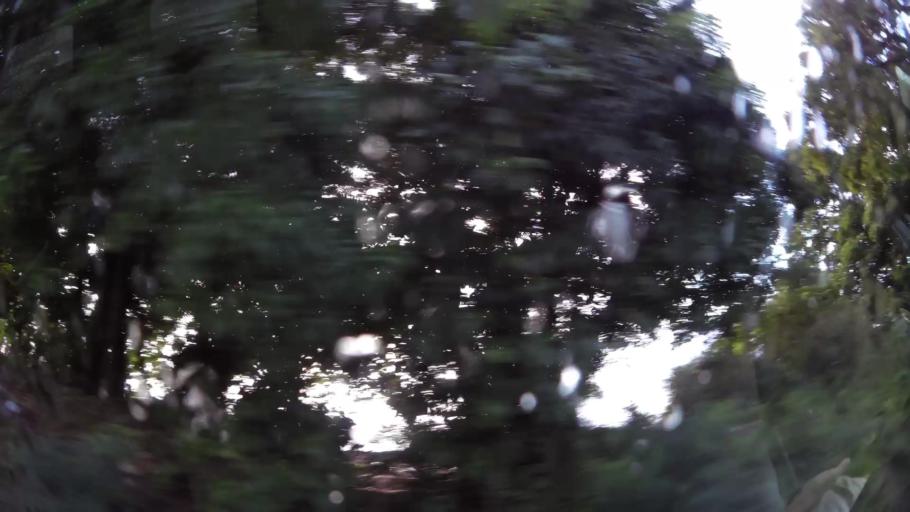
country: DM
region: Saint Paul
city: Mahaut
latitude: 15.3743
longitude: -61.4057
